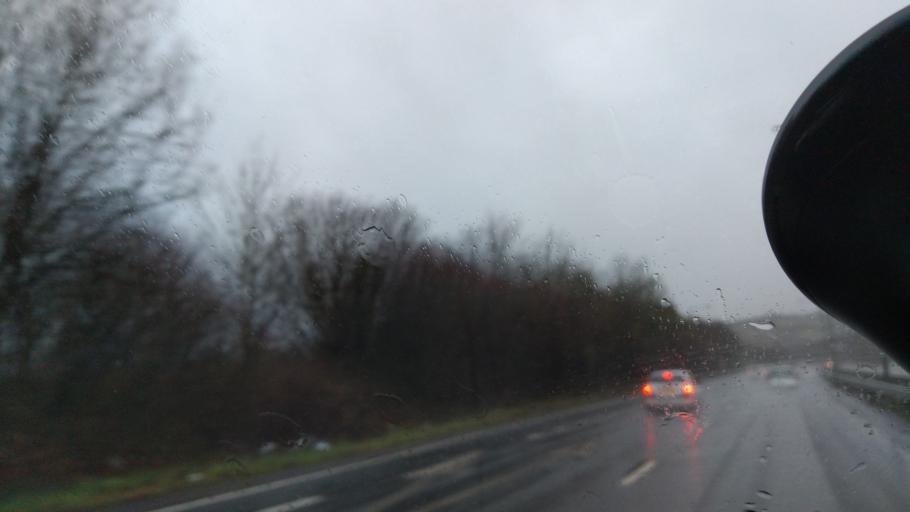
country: GB
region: England
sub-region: Brighton and Hove
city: Brighton
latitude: 50.8690
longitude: -0.1461
